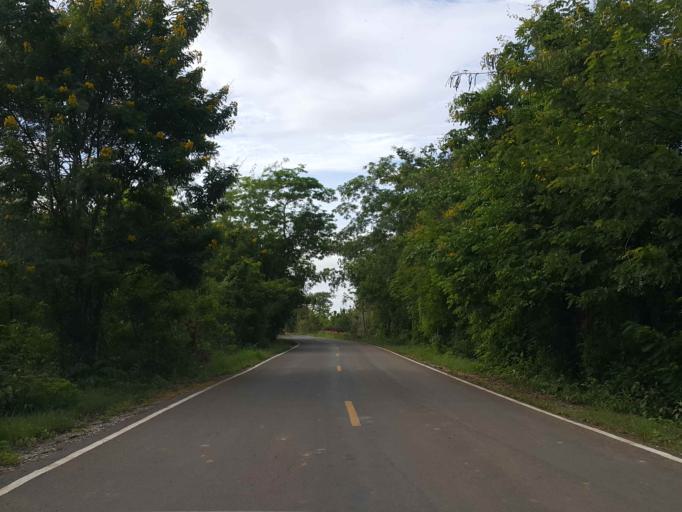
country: TH
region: Sukhothai
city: Thung Saliam
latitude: 17.3084
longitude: 99.5251
